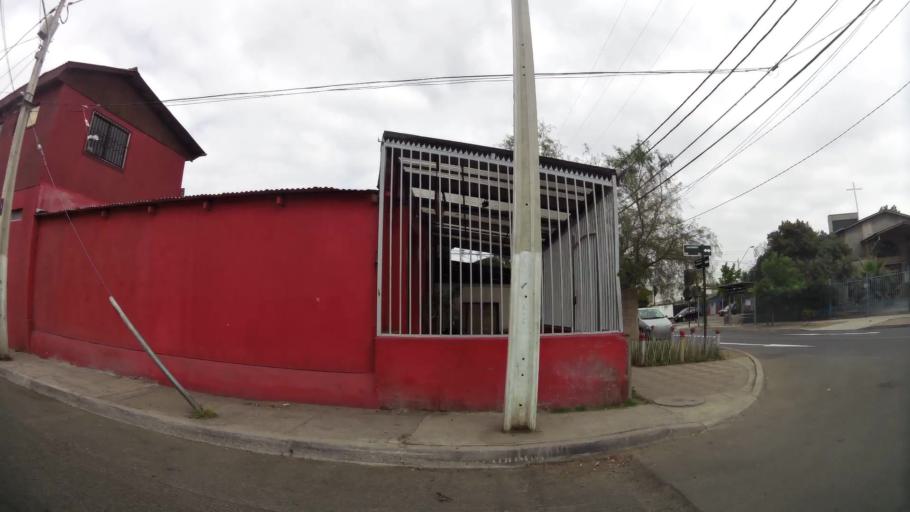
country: CL
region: Santiago Metropolitan
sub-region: Provincia de Maipo
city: San Bernardo
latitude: -33.5224
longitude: -70.6903
